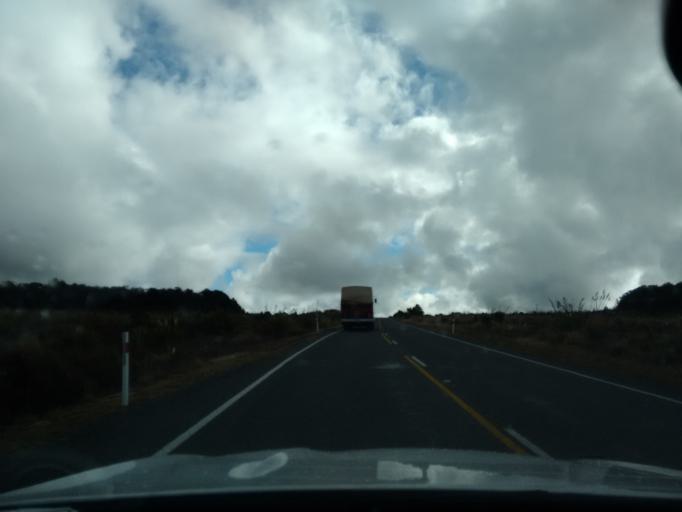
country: NZ
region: Manawatu-Wanganui
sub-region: Ruapehu District
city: Waiouru
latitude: -39.1783
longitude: 175.4657
